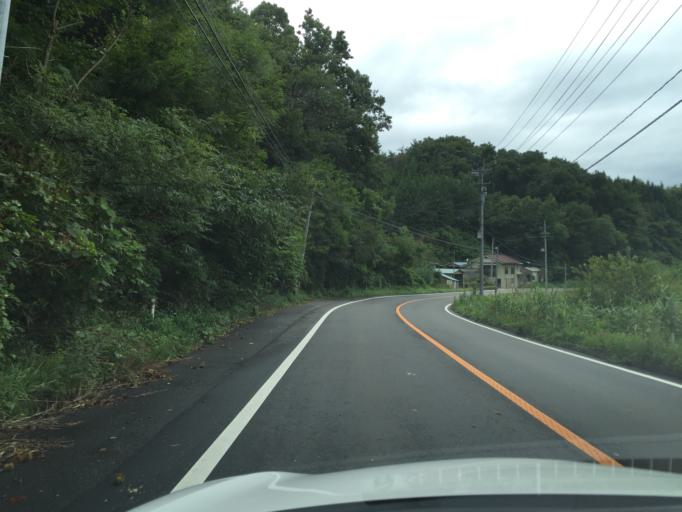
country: JP
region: Fukushima
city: Funehikimachi-funehiki
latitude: 37.4655
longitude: 140.5709
